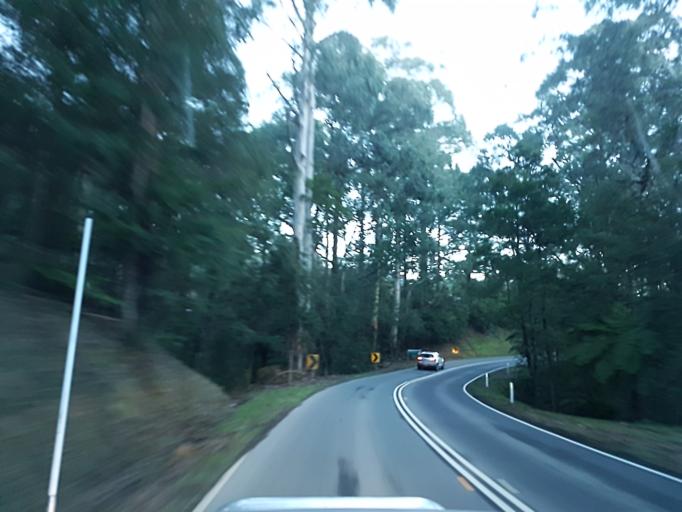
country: AU
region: Victoria
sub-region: Yarra Ranges
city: Millgrove
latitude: -37.7331
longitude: 145.7446
